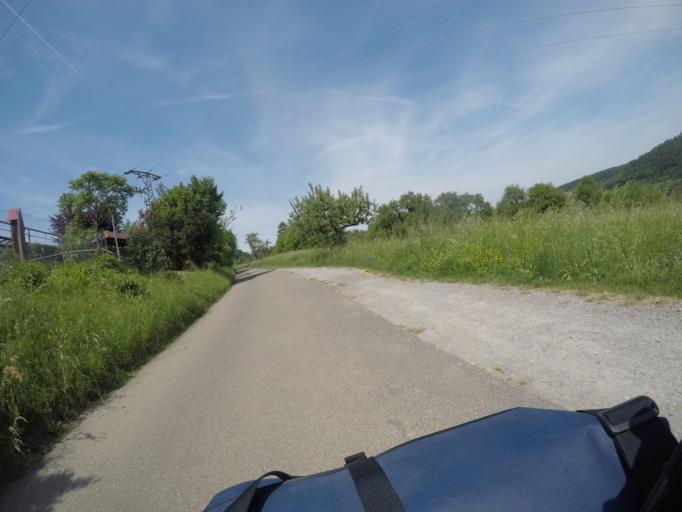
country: DE
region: Baden-Wuerttemberg
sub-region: Karlsruhe Region
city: Konigsbach-Stein
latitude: 48.9370
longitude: 8.6258
